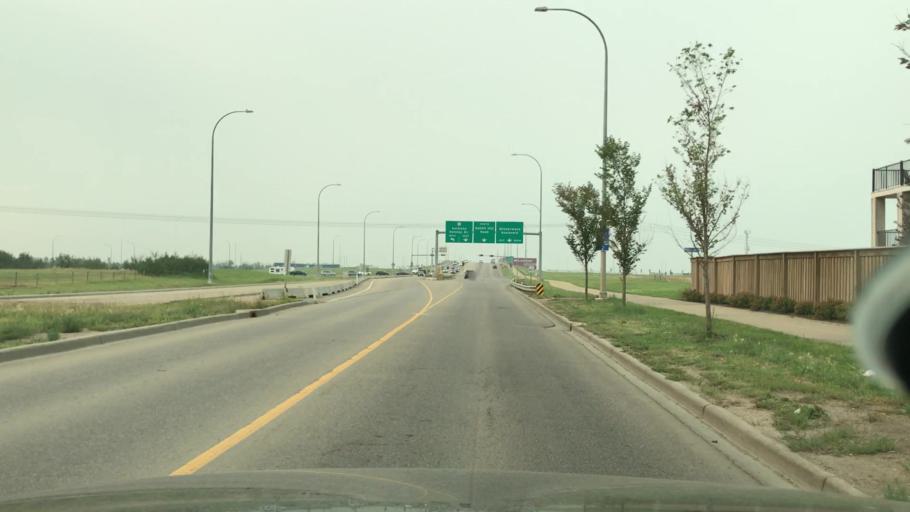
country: CA
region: Alberta
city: Edmonton
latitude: 53.4341
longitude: -113.5769
